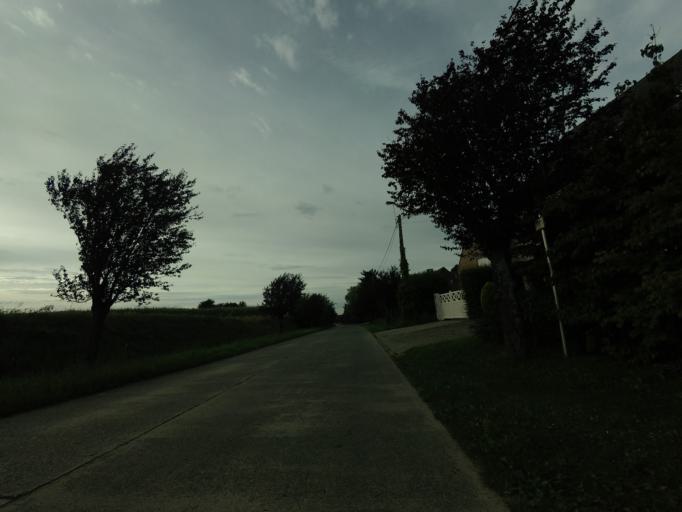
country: BE
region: Flanders
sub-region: Provincie Vlaams-Brabant
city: Grimbergen
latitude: 50.9641
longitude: 4.3614
